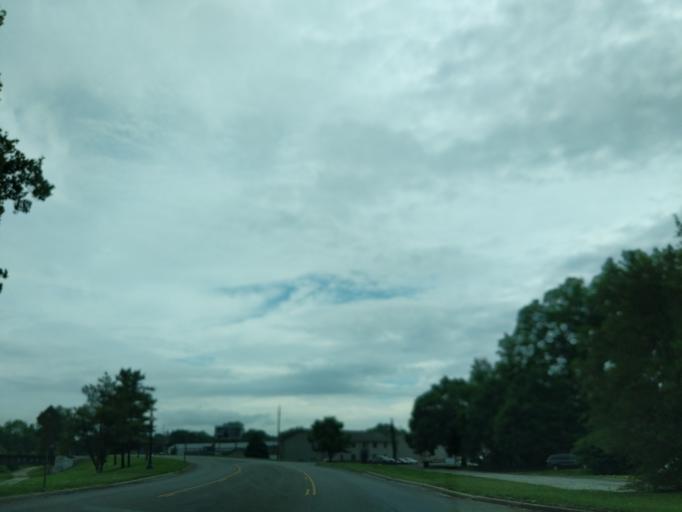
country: US
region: Indiana
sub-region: Delaware County
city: Muncie
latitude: 40.1901
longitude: -85.4087
